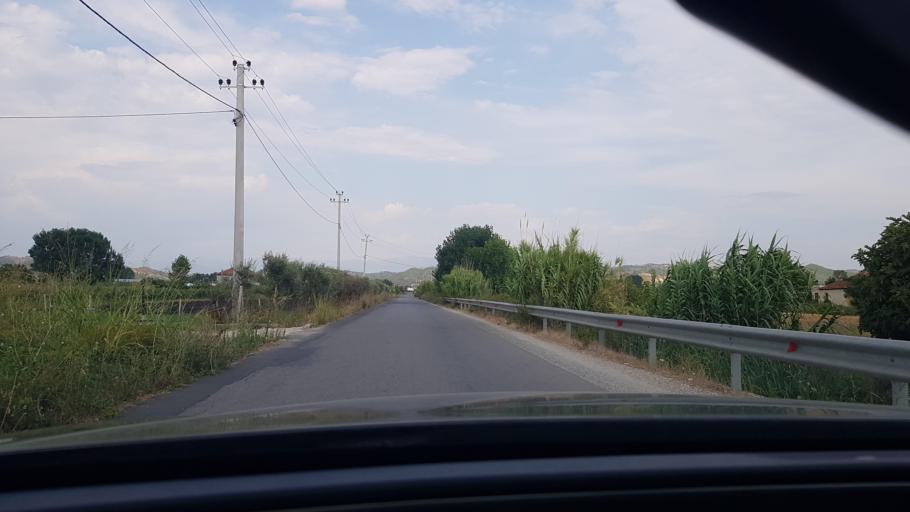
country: AL
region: Durres
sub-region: Rrethi i Durresit
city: Manze
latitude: 41.4724
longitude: 19.5416
